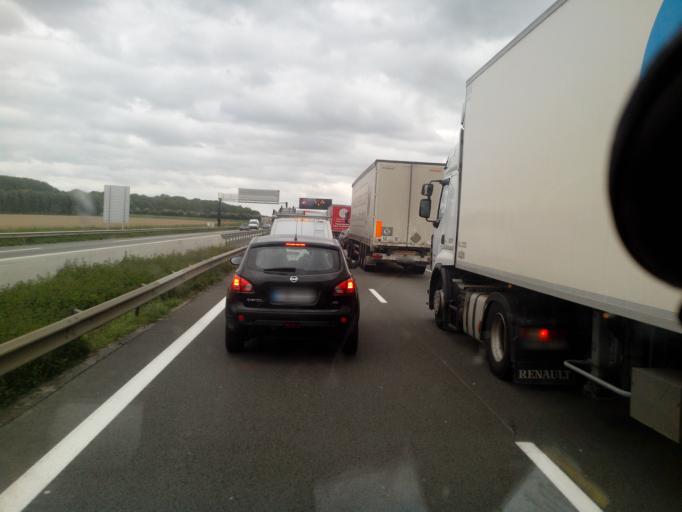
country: FR
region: Nord-Pas-de-Calais
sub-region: Departement du Nord
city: Ennetieres-en-Weppes
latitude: 50.6358
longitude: 2.9449
